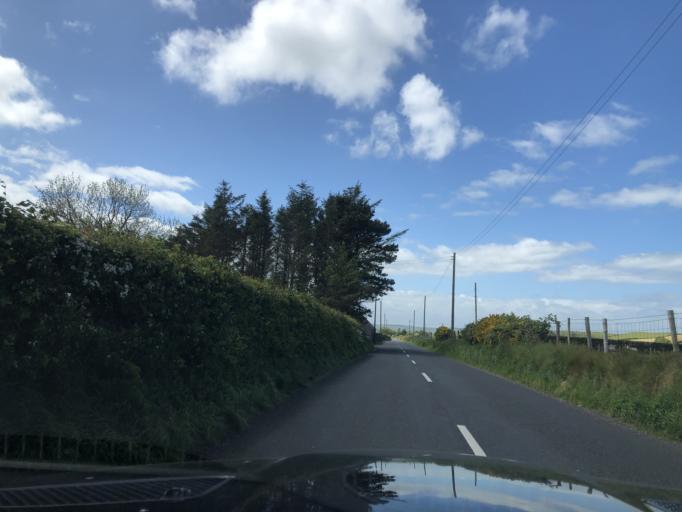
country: GB
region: Northern Ireland
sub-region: Moyle District
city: Ballycastle
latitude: 55.1998
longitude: -6.1756
